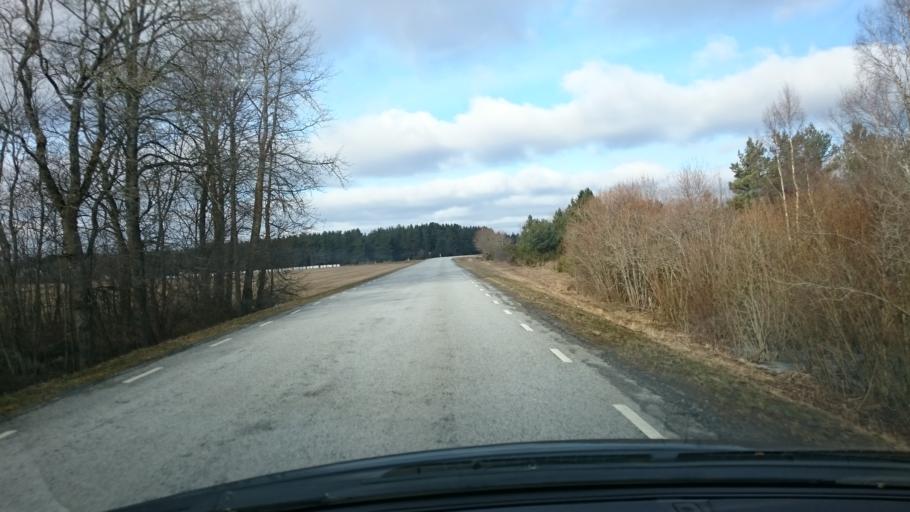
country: EE
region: Harju
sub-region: Keila linn
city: Keila
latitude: 59.3557
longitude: 24.3434
